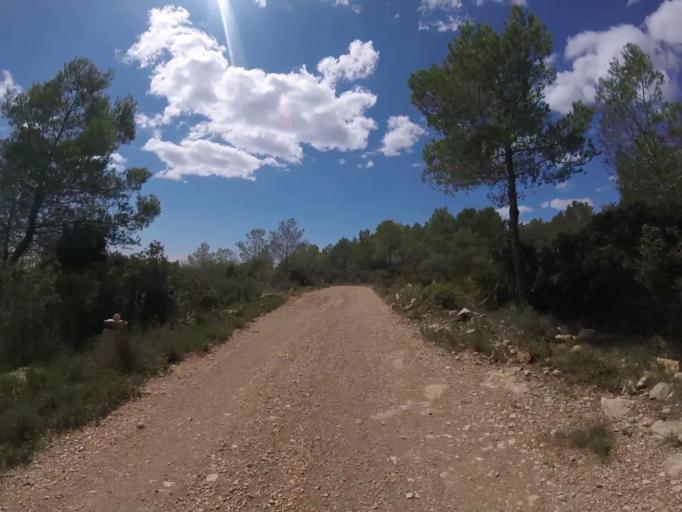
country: ES
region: Valencia
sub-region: Provincia de Castello
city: Alcoceber
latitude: 40.2887
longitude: 0.3182
